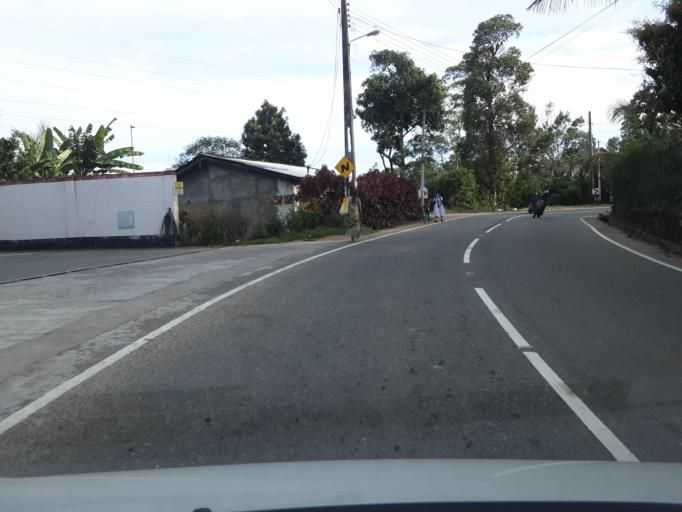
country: LK
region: Uva
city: Badulla
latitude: 6.9372
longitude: 80.9931
